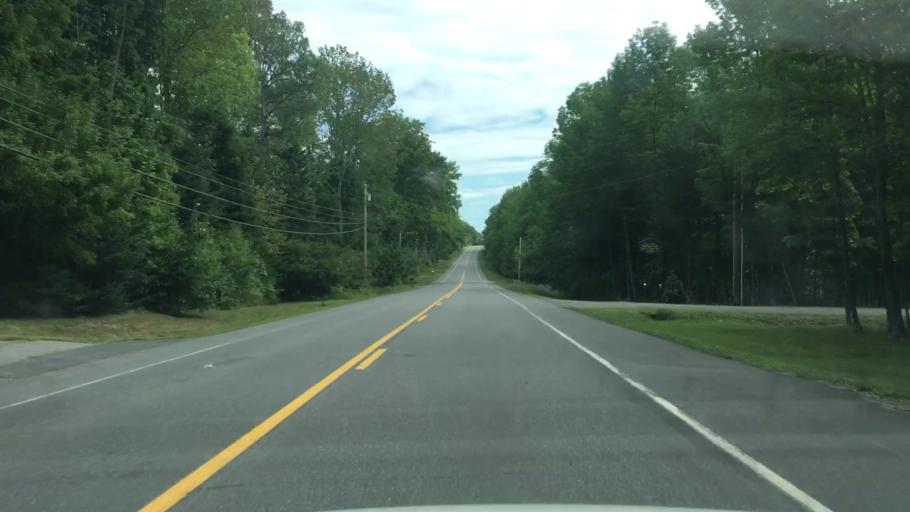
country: US
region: Maine
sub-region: Piscataquis County
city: Brownville
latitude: 45.2268
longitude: -69.1152
